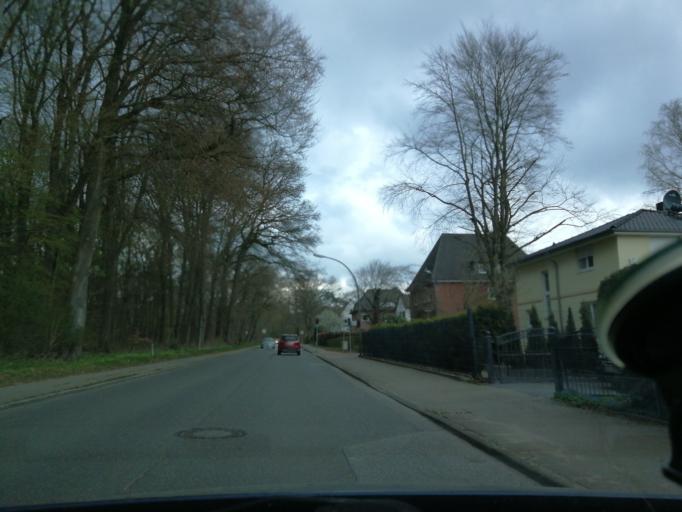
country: DE
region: Hamburg
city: Harburg
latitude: 53.4586
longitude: 9.9352
